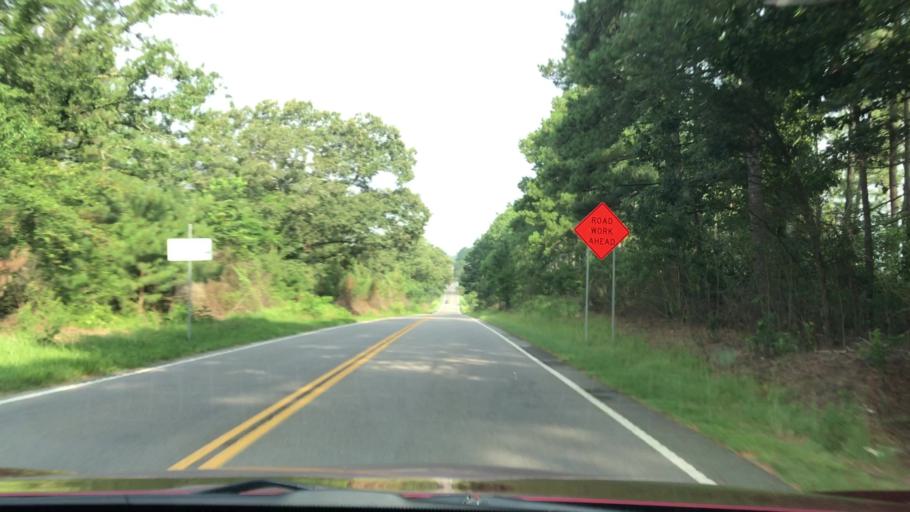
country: US
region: South Carolina
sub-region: Lexington County
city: Leesville
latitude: 33.6855
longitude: -81.4558
